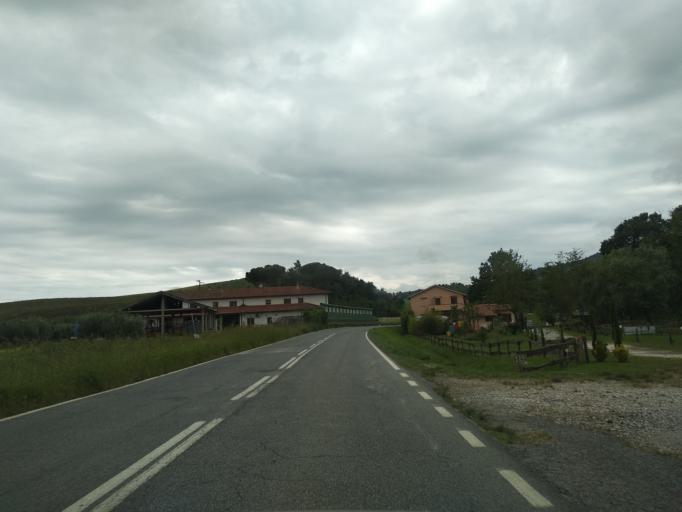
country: IT
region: Tuscany
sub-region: Provincia di Livorno
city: Collesalvetti
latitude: 43.5357
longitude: 10.4626
